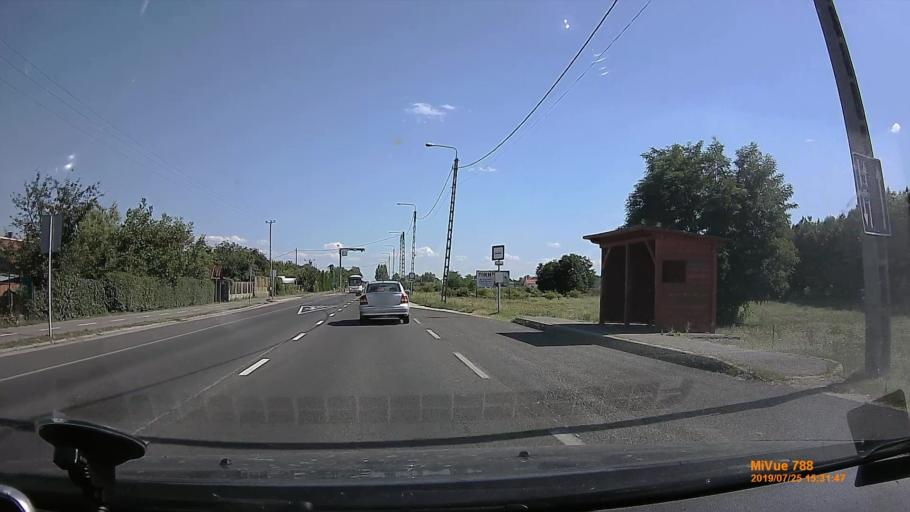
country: HU
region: Borsod-Abauj-Zemplen
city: Malyi
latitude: 48.0112
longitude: 20.8256
